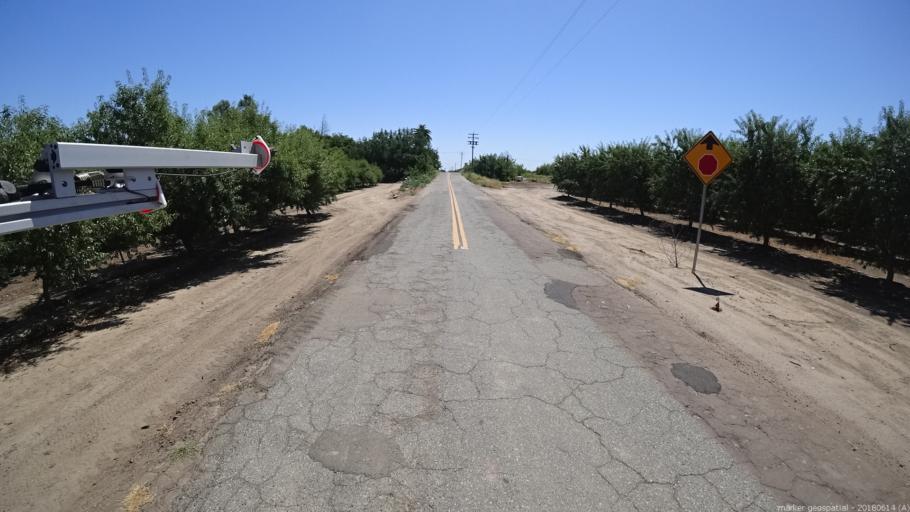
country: US
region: California
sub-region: Madera County
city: Fairmead
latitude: 36.9892
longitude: -120.2044
